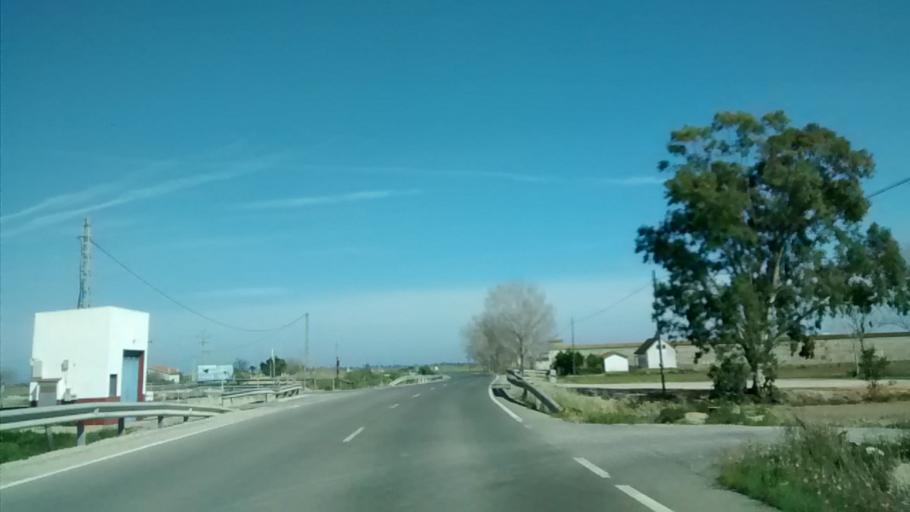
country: ES
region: Catalonia
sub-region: Provincia de Tarragona
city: Deltebre
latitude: 40.7049
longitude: 0.7857
